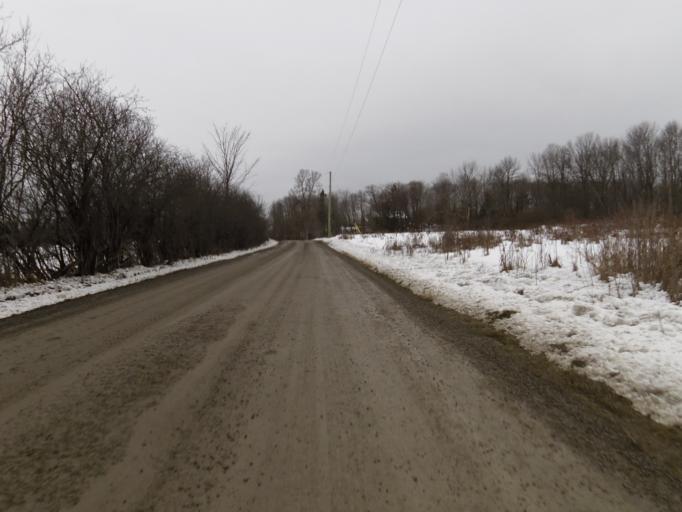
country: CA
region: Ontario
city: Carleton Place
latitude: 45.1958
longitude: -76.2158
